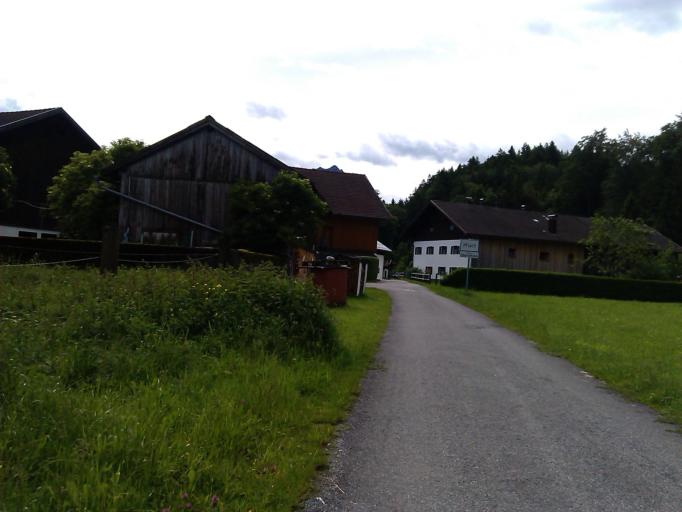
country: AT
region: Tyrol
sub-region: Politischer Bezirk Reutte
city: Pflach
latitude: 47.5123
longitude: 10.7058
